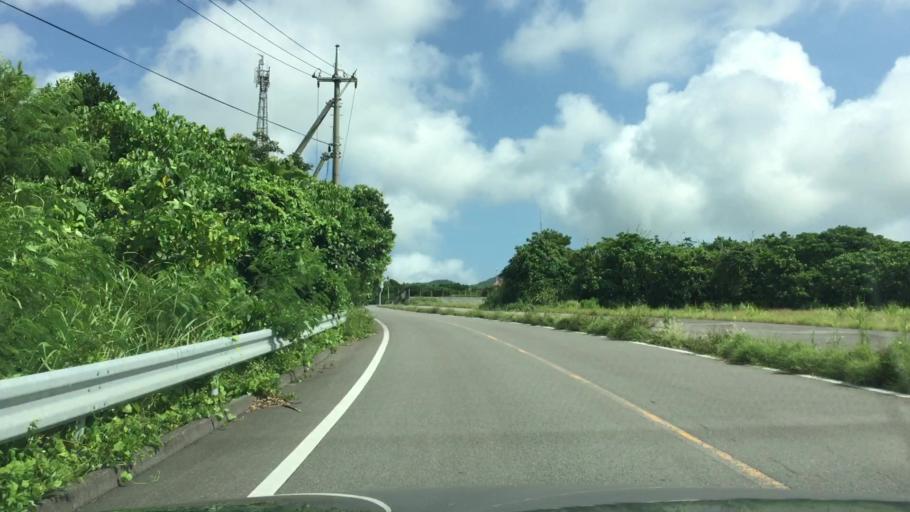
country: JP
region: Okinawa
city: Ishigaki
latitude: 24.4190
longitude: 124.2149
